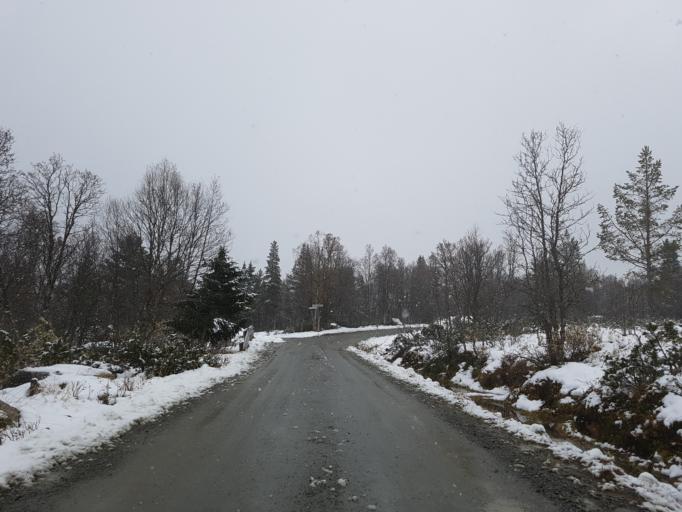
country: NO
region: Oppland
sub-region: Sel
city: Otta
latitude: 61.7903
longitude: 9.7192
